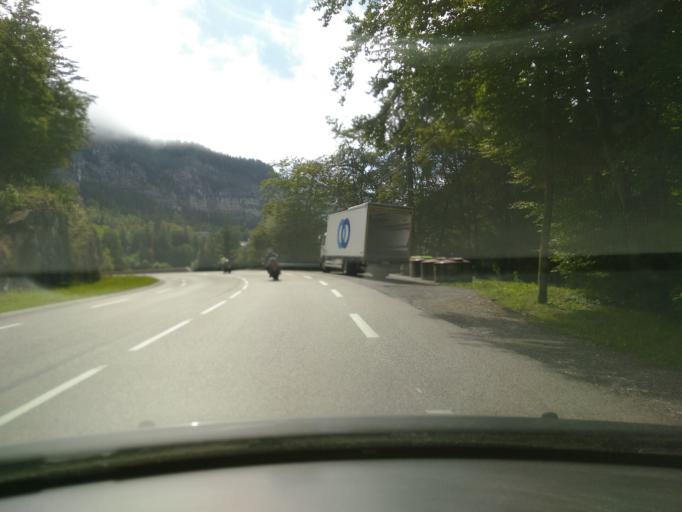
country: FR
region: Rhone-Alpes
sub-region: Departement de la Haute-Savoie
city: Saint-Jean-de-Sixt
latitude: 45.9197
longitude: 6.4154
